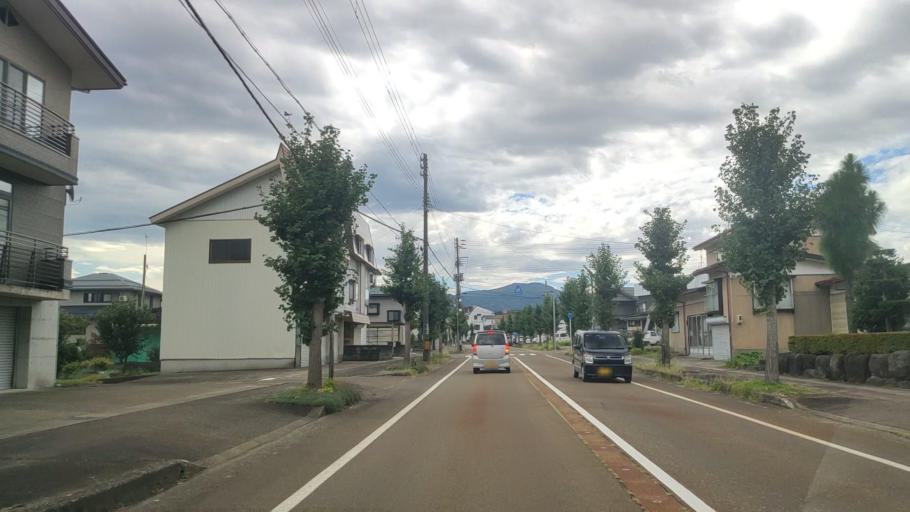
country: JP
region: Niigata
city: Arai
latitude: 37.0227
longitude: 138.2464
